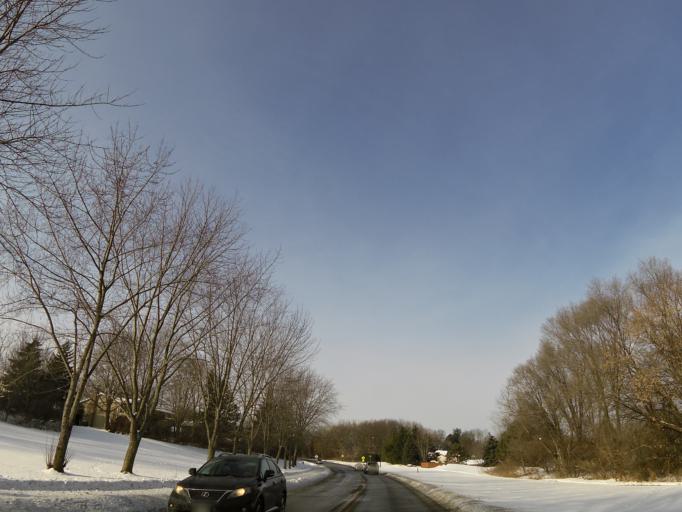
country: US
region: Minnesota
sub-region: Hennepin County
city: Eden Prairie
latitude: 44.8435
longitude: -93.4336
